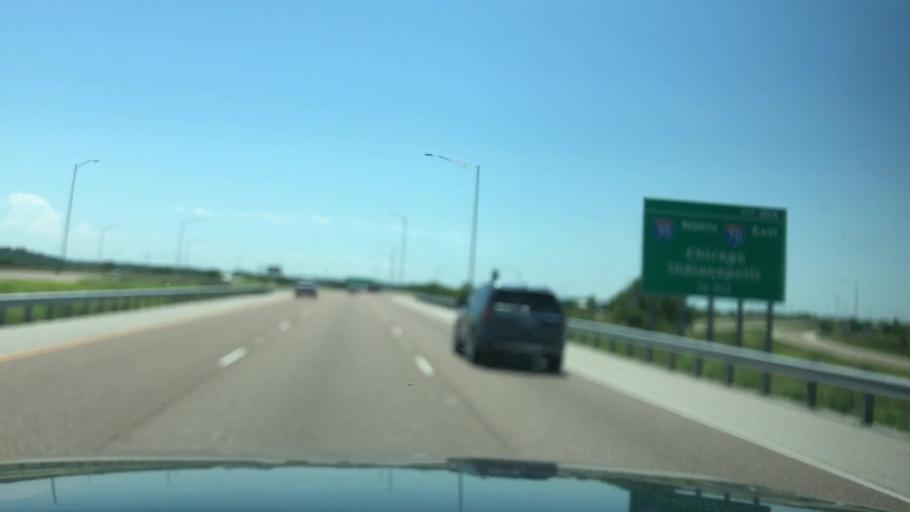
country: US
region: Illinois
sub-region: Saint Clair County
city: Caseyville
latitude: 38.6774
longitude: -90.0300
